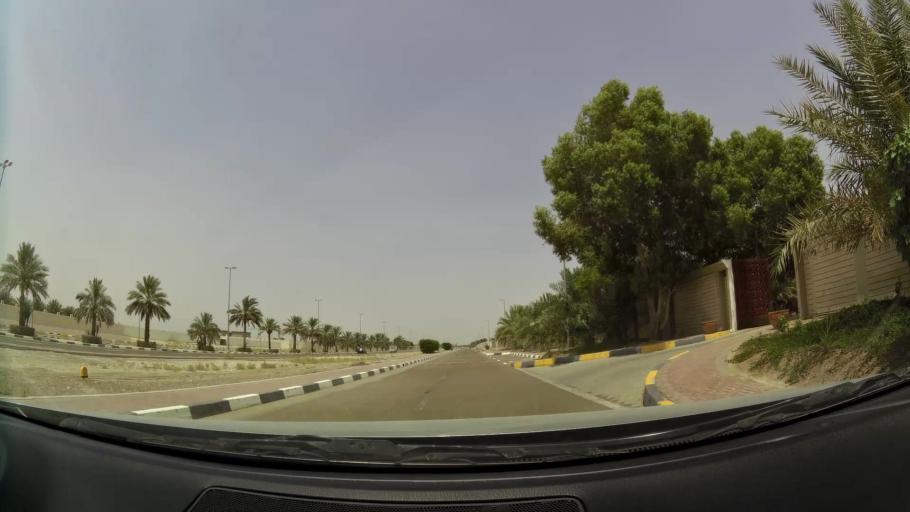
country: AE
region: Abu Dhabi
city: Al Ain
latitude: 24.1853
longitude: 55.6821
